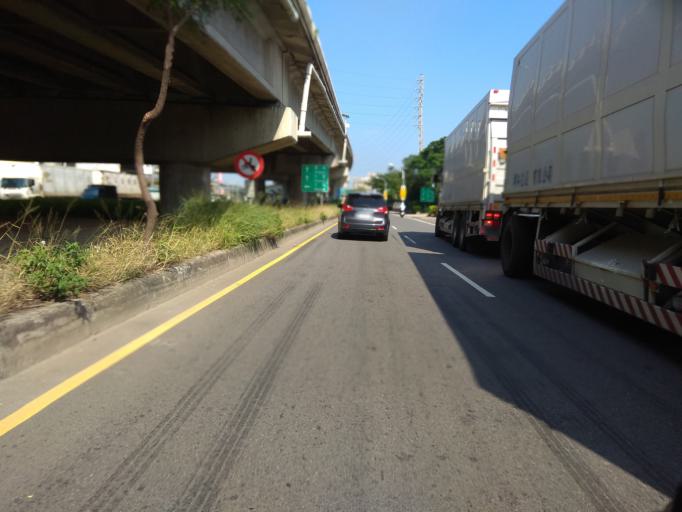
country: TW
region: Taiwan
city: Taoyuan City
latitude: 24.9848
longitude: 121.2379
